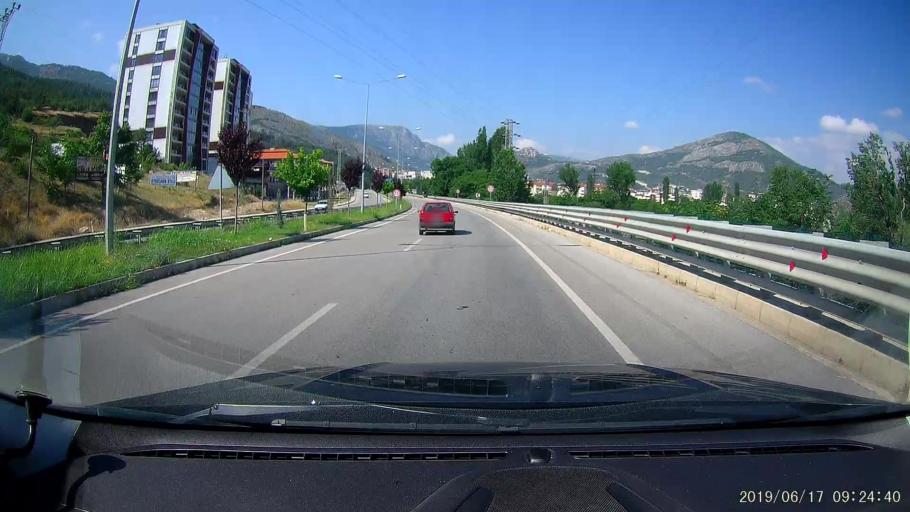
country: TR
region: Amasya
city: Amasya
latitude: 40.6709
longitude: 35.8545
